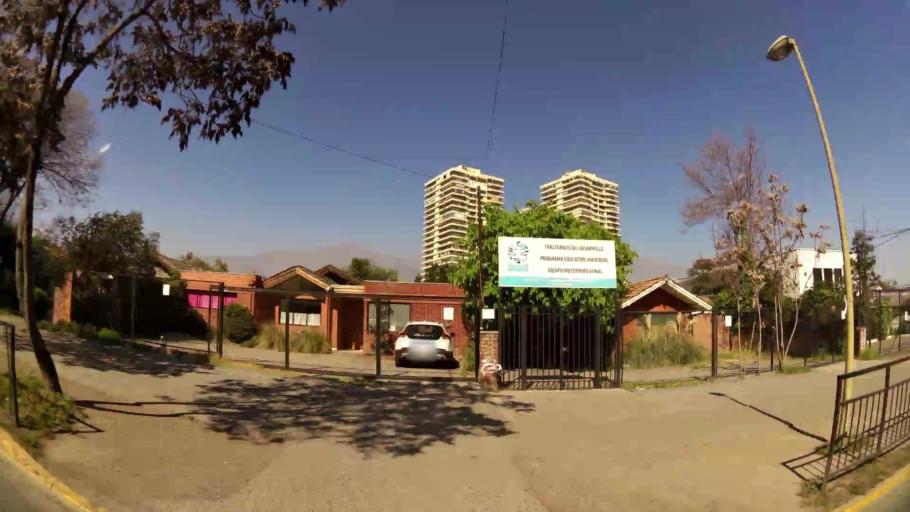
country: CL
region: Santiago Metropolitan
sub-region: Provincia de Santiago
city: Villa Presidente Frei, Nunoa, Santiago, Chile
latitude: -33.4065
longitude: -70.5507
